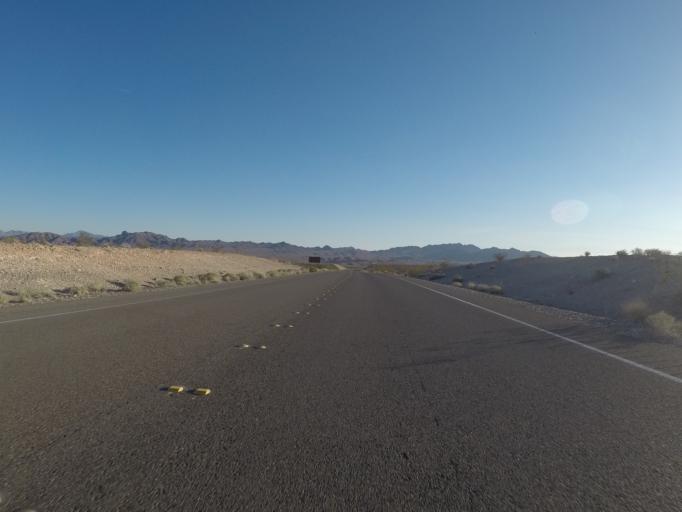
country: US
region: Nevada
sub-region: Clark County
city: Moapa Valley
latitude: 36.3292
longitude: -114.4927
